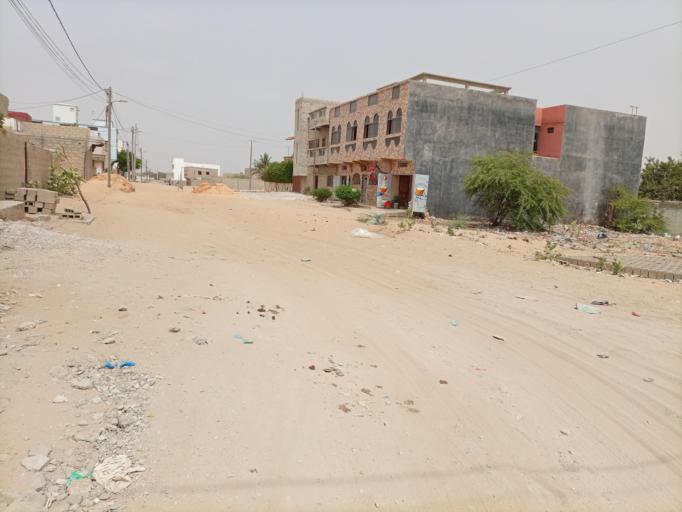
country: SN
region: Saint-Louis
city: Saint-Louis
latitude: 16.0396
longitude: -16.4417
